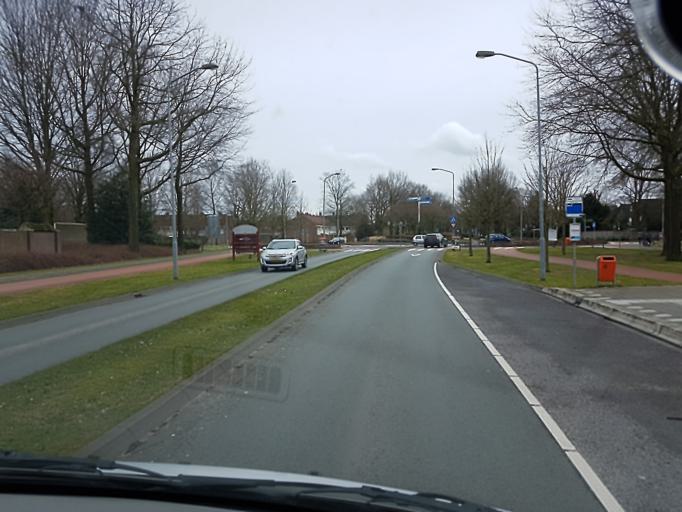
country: NL
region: North Brabant
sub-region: Gemeente Veldhoven
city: Veldhoven
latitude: 51.4226
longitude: 5.3922
